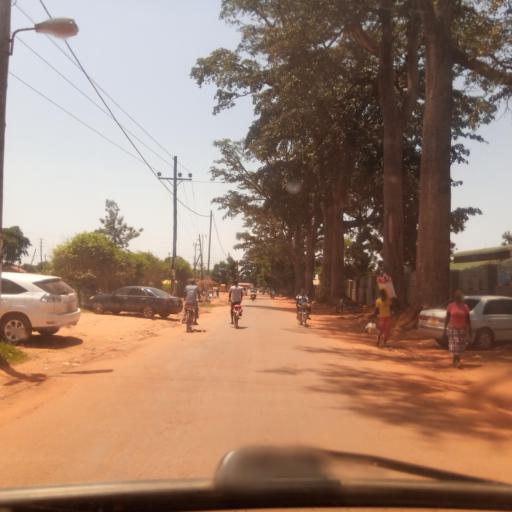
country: UG
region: Northern Region
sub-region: Lira District
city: Lira
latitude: 2.2522
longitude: 32.9007
